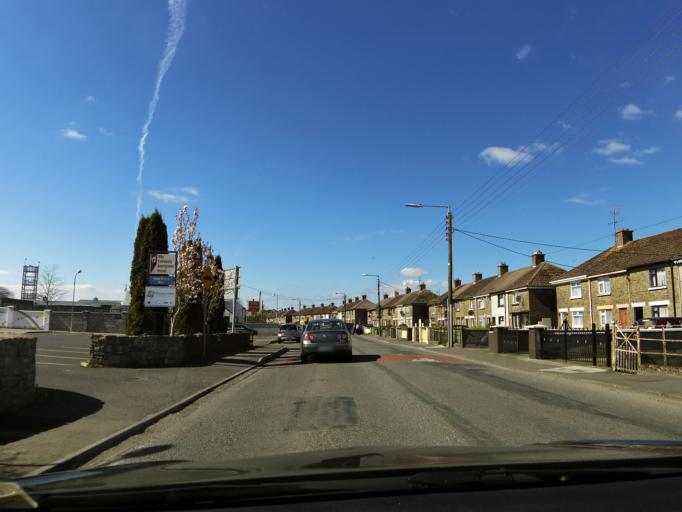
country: IE
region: Leinster
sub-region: Kildare
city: Athy
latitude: 52.9957
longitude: -6.9918
